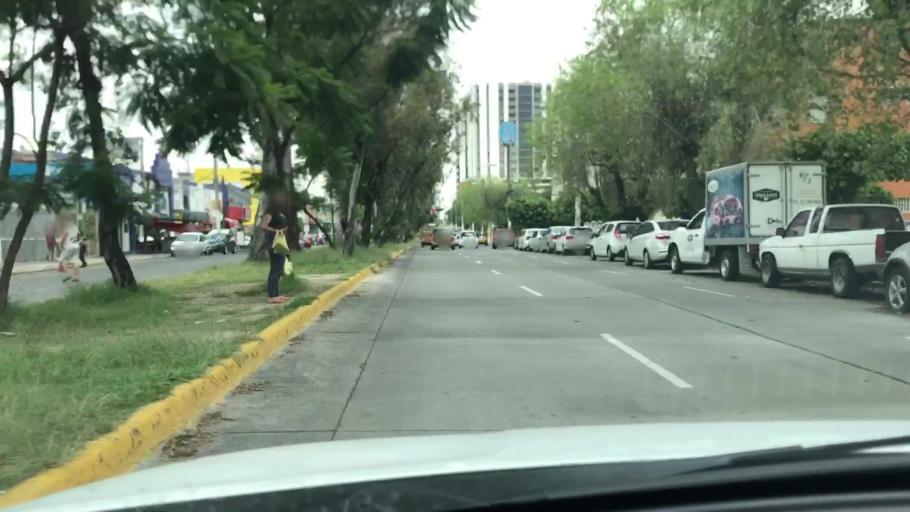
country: MX
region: Jalisco
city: Guadalajara
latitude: 20.6549
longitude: -103.4323
